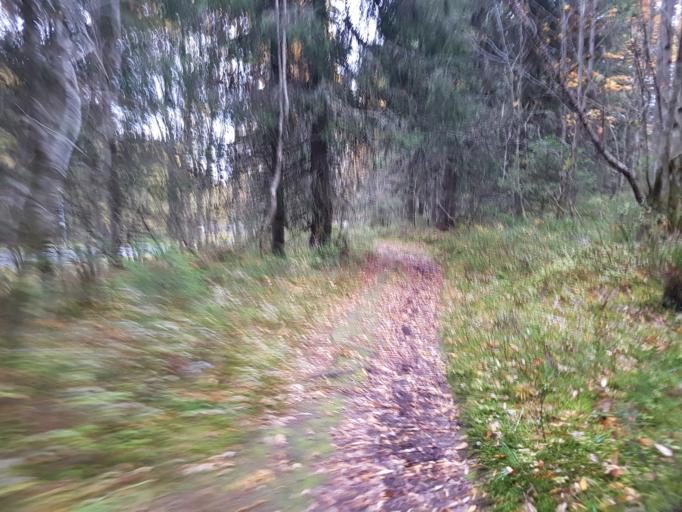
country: NO
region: Sor-Trondelag
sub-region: Trondheim
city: Trondheim
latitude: 63.3802
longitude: 10.3331
